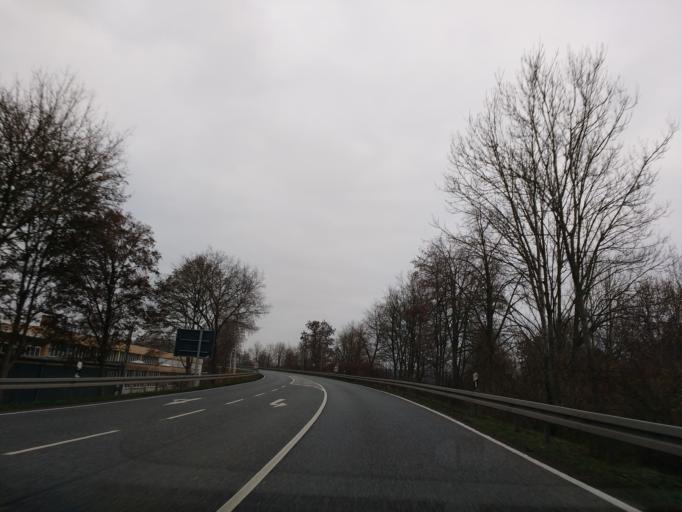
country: DE
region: Hesse
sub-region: Regierungsbezirk Kassel
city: Alheim
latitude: 51.0663
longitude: 9.6107
